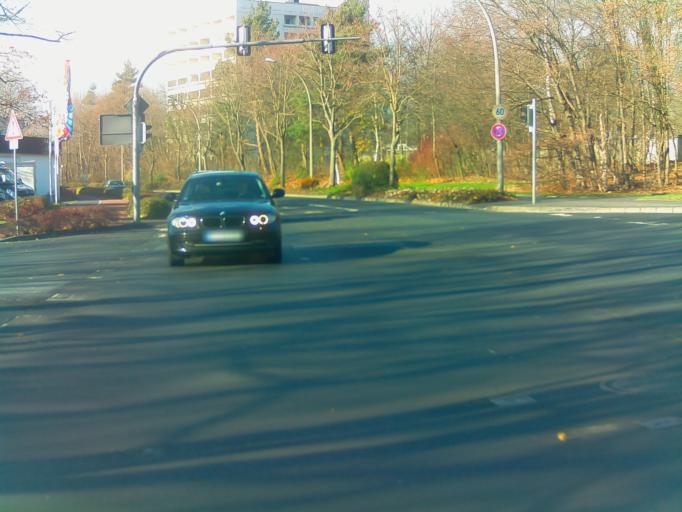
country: DE
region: Bavaria
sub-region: Regierungsbezirk Unterfranken
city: Bad Kissingen
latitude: 50.2045
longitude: 10.0876
